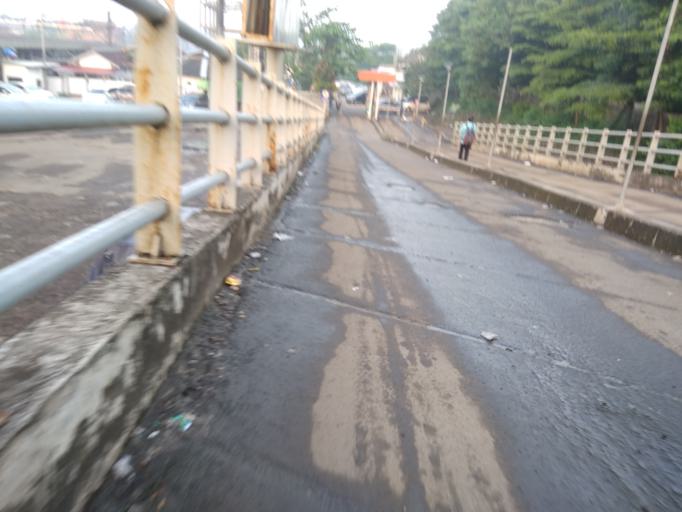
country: ID
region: West Java
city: Serpong
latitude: -6.3144
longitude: 106.6765
